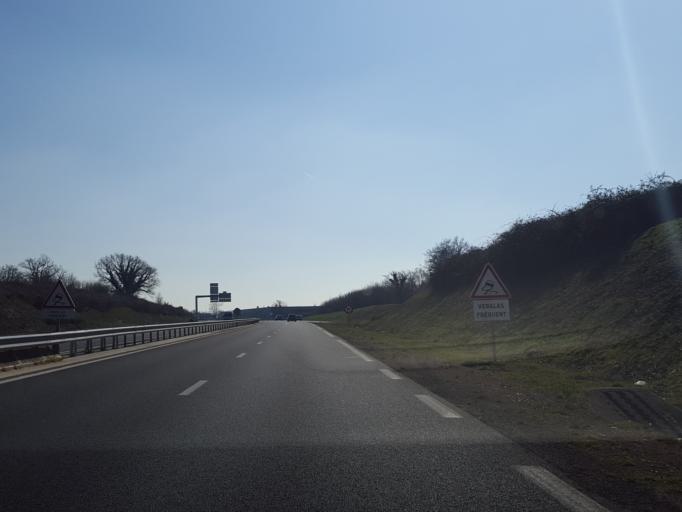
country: FR
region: Pays de la Loire
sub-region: Departement de la Vendee
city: La Ferriere
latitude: 46.6714
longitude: -1.3602
